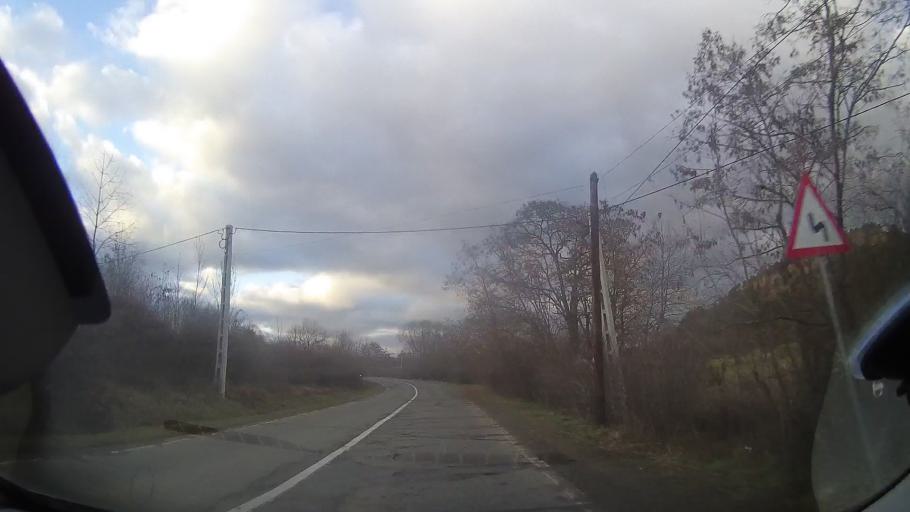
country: RO
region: Cluj
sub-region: Comuna Calatele
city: Calatele
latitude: 46.7850
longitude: 23.0034
